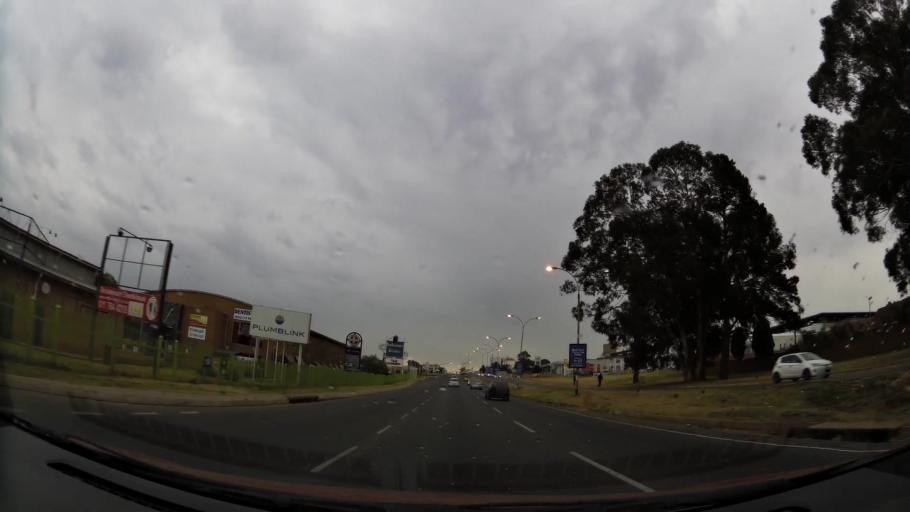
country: ZA
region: Gauteng
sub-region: City of Johannesburg Metropolitan Municipality
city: Roodepoort
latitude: -26.1308
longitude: 27.8528
